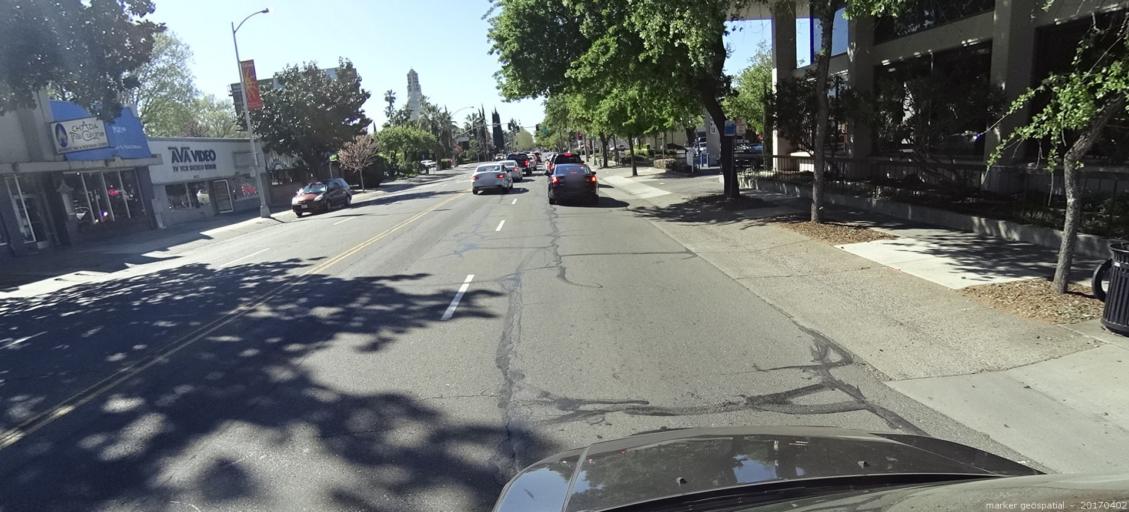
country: US
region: California
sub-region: Sacramento County
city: Sacramento
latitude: 38.5613
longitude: -121.4912
